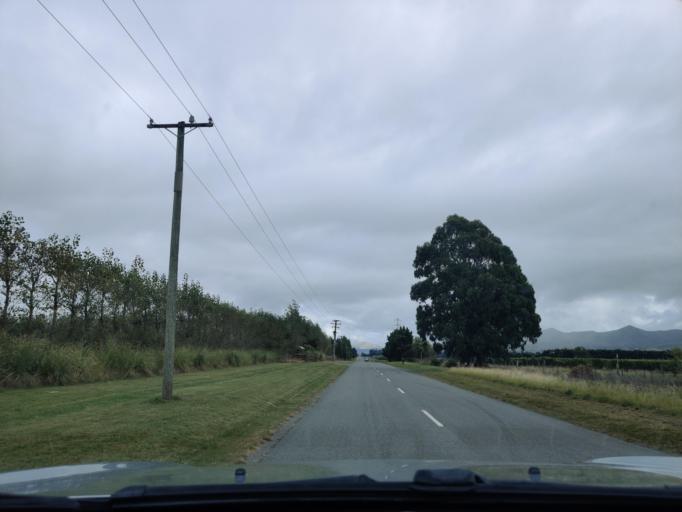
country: NZ
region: Canterbury
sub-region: Hurunui District
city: Amberley
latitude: -43.0766
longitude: 172.7111
